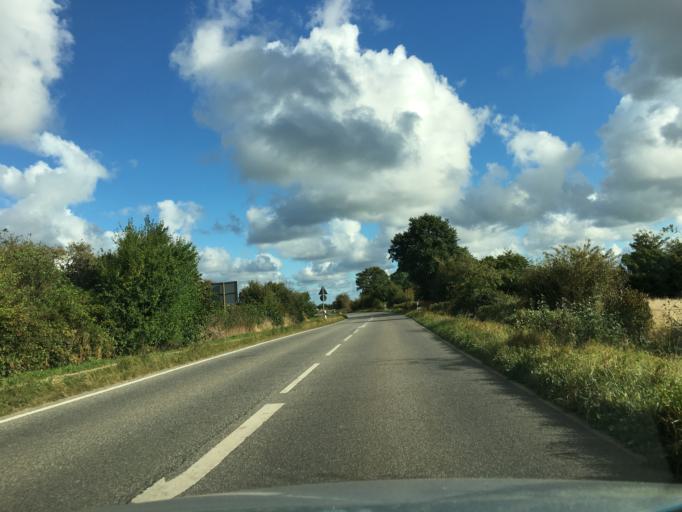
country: DE
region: Schleswig-Holstein
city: Laboe
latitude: 54.4102
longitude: 10.2354
